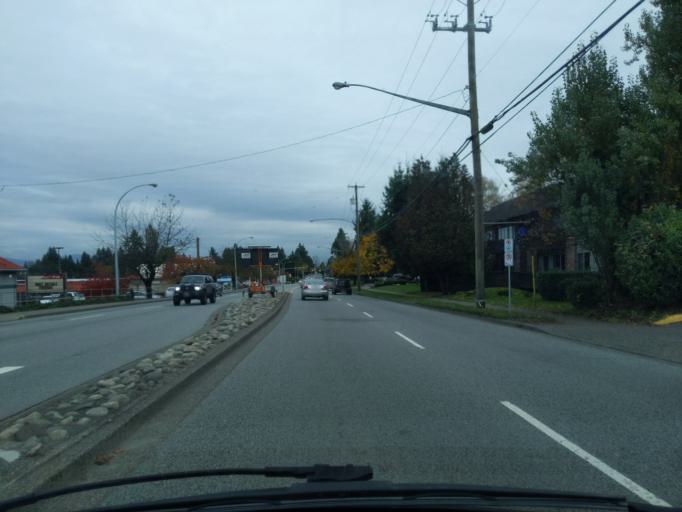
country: CA
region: British Columbia
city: Surrey
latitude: 49.1987
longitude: -122.8120
